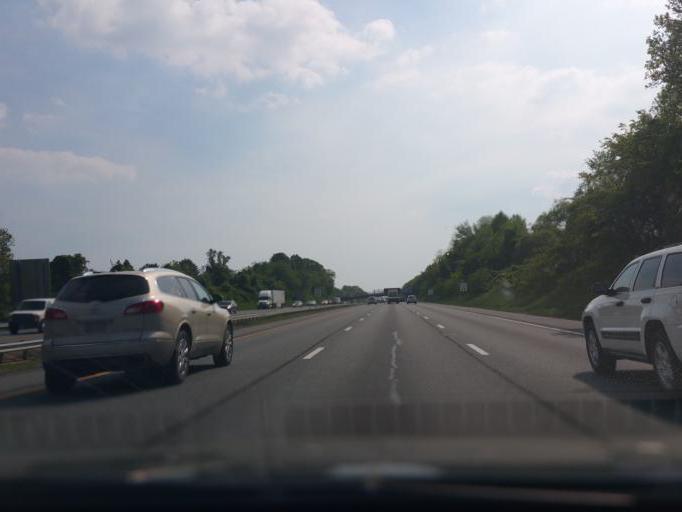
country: US
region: Maryland
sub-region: Harford County
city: Aberdeen
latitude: 39.5172
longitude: -76.2029
